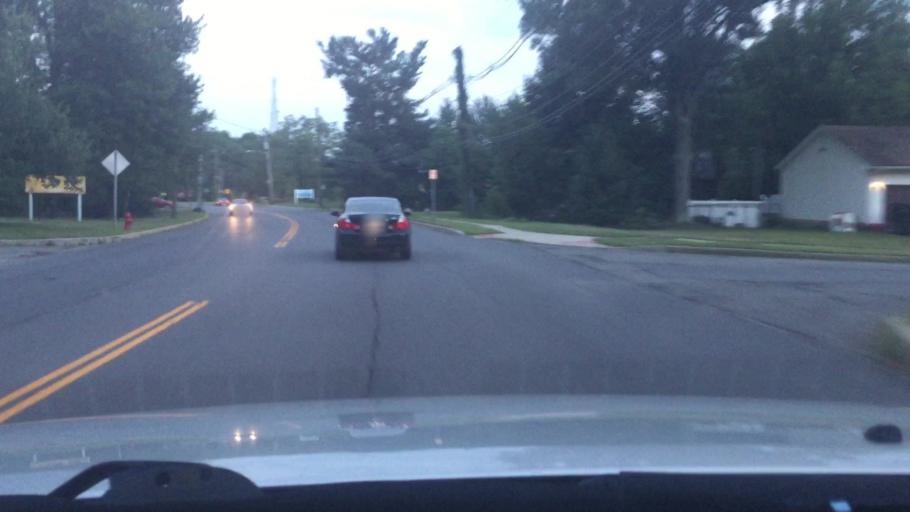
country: US
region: New Jersey
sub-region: Middlesex County
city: East Brunswick
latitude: 40.4208
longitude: -74.4209
